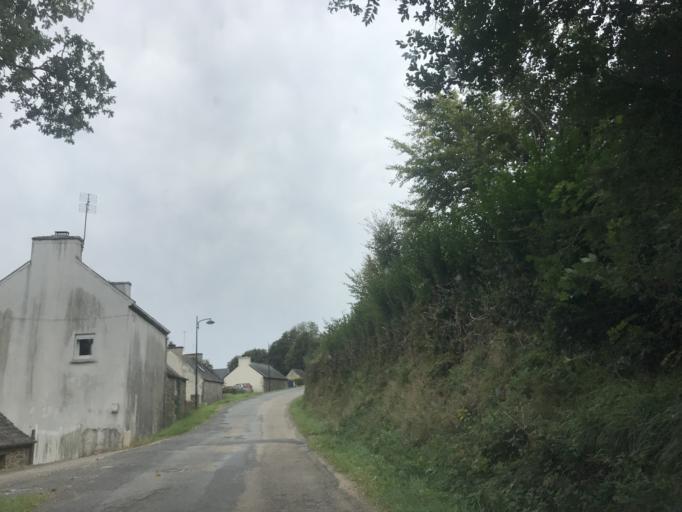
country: FR
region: Brittany
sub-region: Departement du Finistere
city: Plouneour-Menez
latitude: 48.3836
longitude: -3.9125
